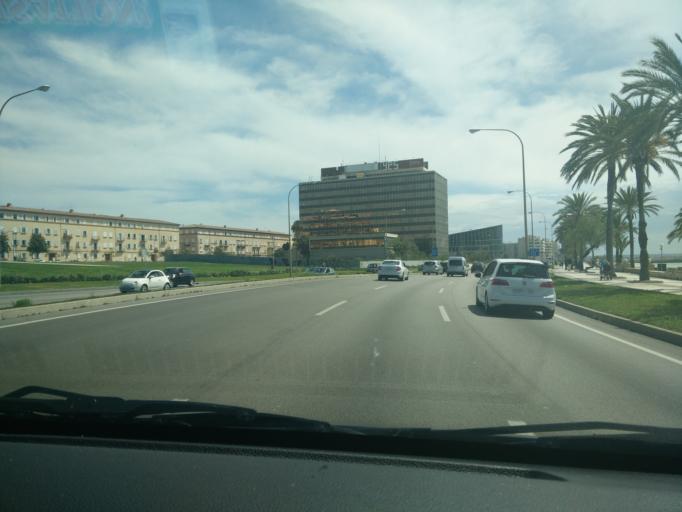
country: ES
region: Balearic Islands
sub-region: Illes Balears
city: Palma
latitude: 39.5643
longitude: 2.6575
